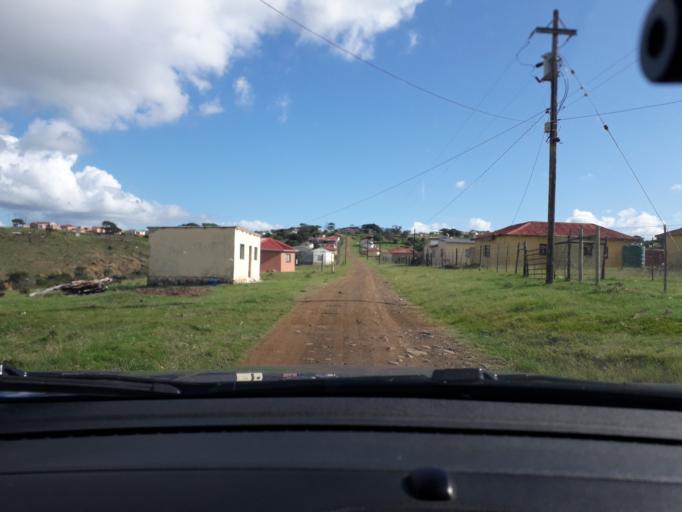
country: ZA
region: Eastern Cape
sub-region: Buffalo City Metropolitan Municipality
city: Bhisho
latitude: -33.1142
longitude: 27.4348
